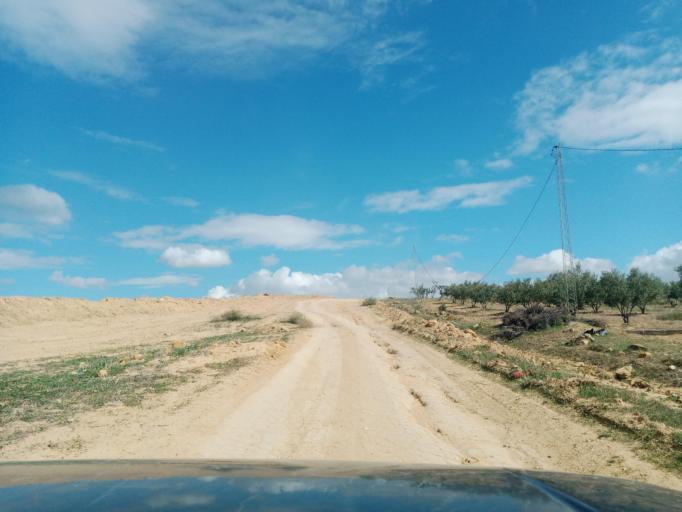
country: TN
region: Tunis
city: Oued Lill
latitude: 36.8076
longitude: 9.9871
